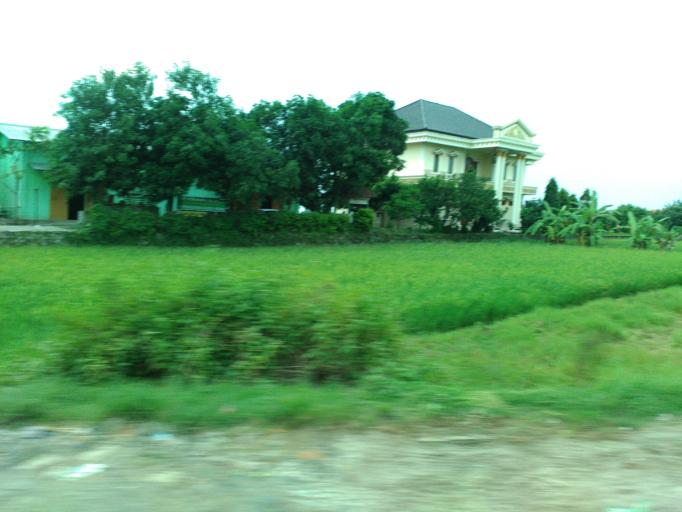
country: ID
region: Central Java
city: Gatak
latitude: -7.5857
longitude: 110.7122
